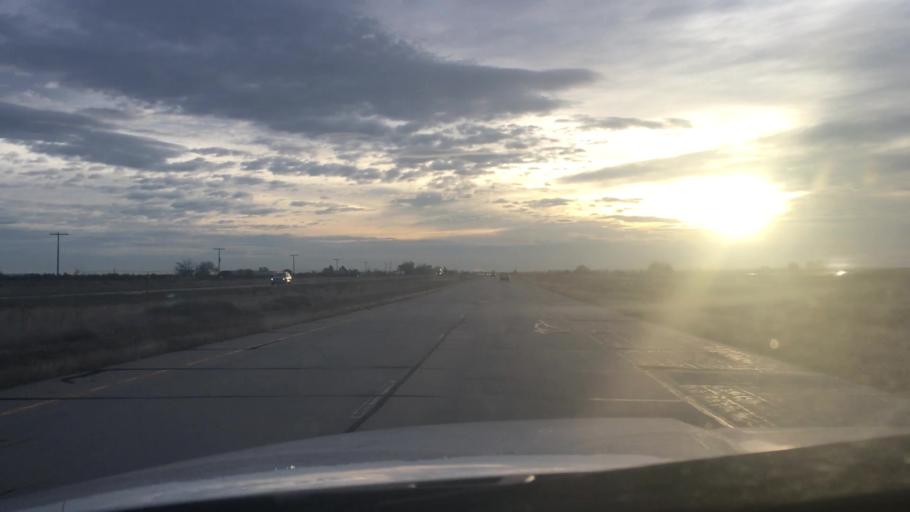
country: US
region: Colorado
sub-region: Morgan County
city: Fort Morgan
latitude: 40.2460
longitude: -103.9746
